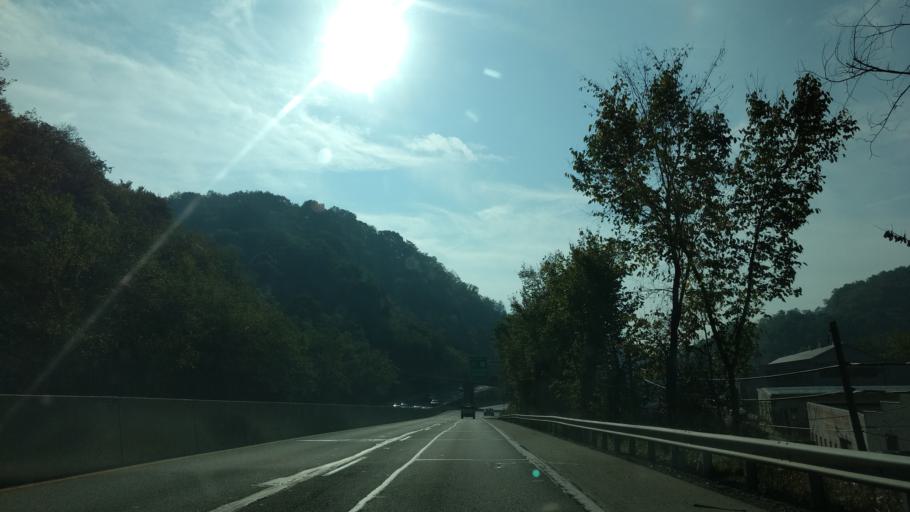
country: US
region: Pennsylvania
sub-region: Allegheny County
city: Green Tree
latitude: 40.4342
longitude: -80.0302
